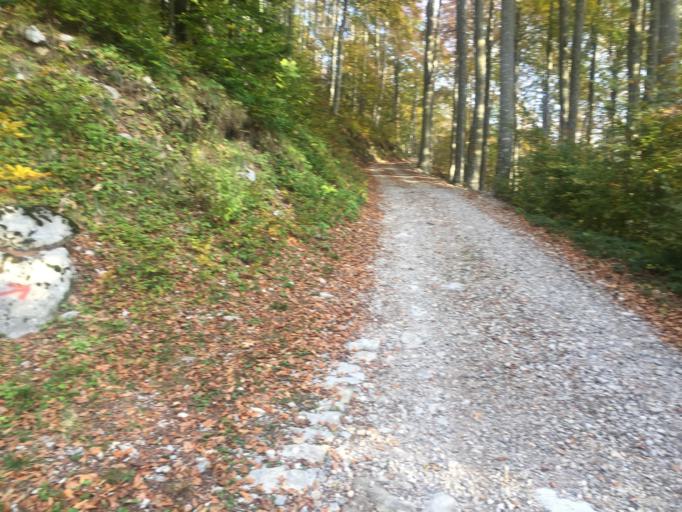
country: IT
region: Friuli Venezia Giulia
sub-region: Provincia di Udine
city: Preone
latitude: 46.3445
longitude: 12.8725
